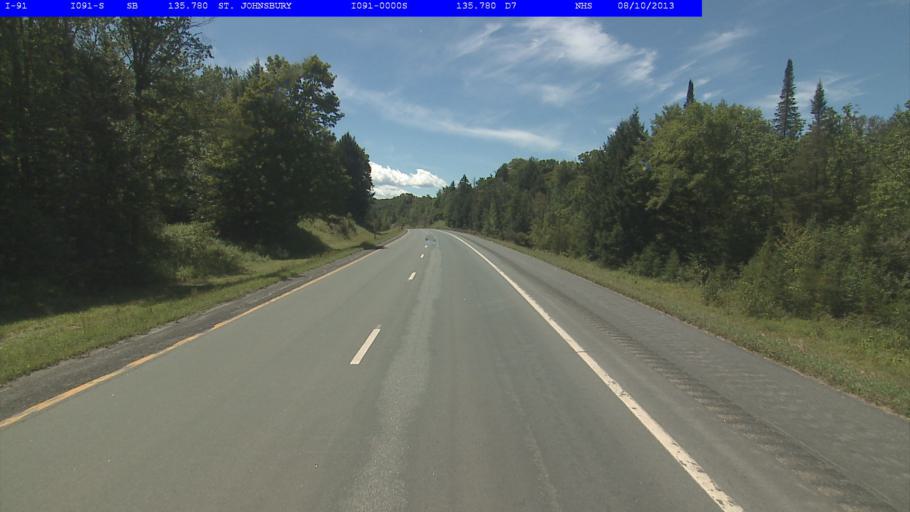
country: US
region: Vermont
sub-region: Caledonia County
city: Lyndon
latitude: 44.5005
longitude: -72.0208
